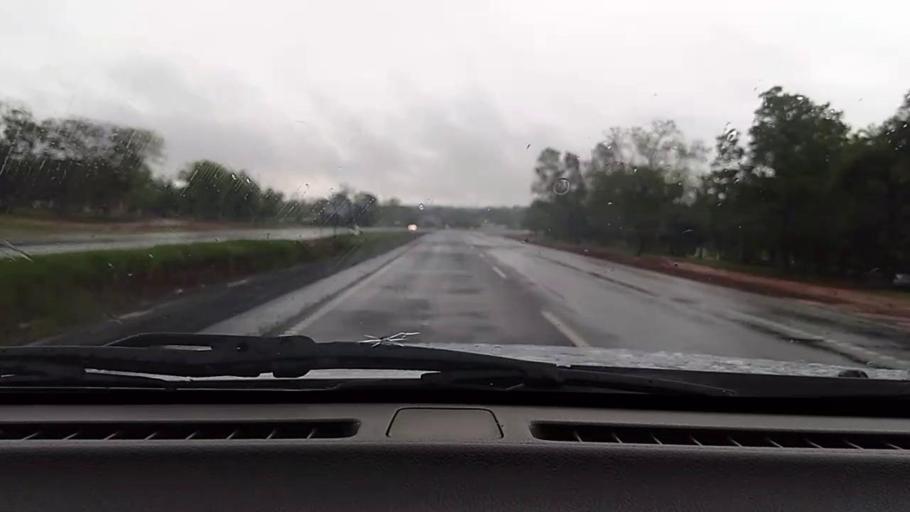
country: PY
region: Caaguazu
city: Repatriacion
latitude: -25.4645
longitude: -55.9312
